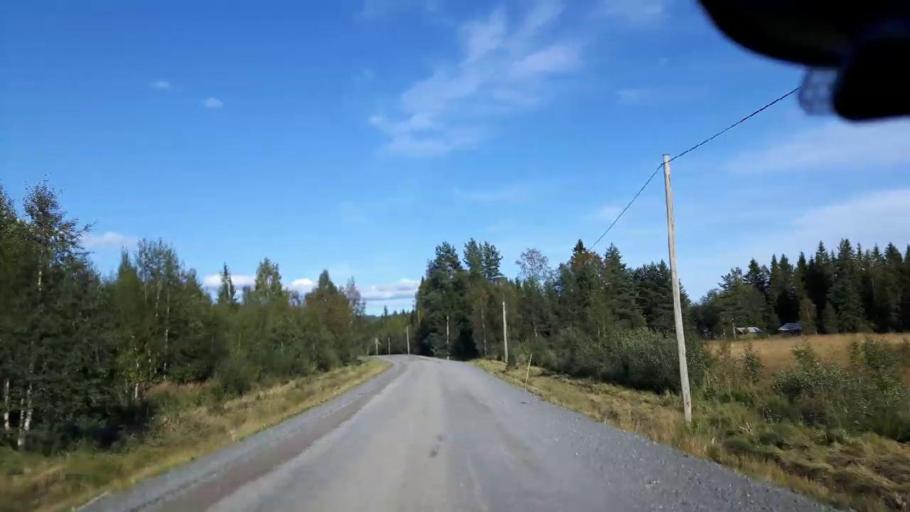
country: SE
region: Vaesternorrland
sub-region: Solleftea Kommun
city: As
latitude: 63.4548
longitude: 16.2379
